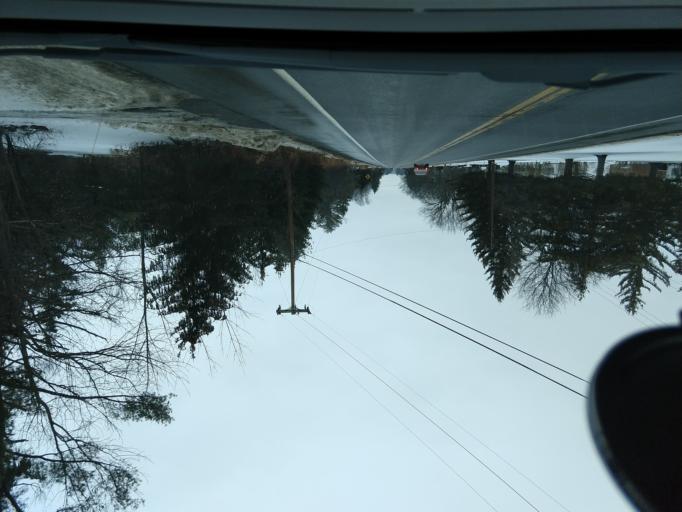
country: US
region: New York
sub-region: Tompkins County
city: Lansing
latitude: 42.5315
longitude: -76.4921
